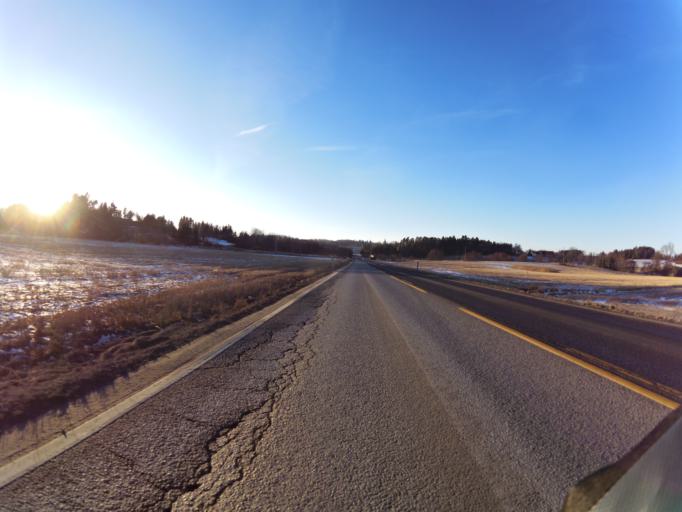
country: NO
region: Ostfold
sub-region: Fredrikstad
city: Fredrikstad
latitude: 59.2522
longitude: 10.8719
